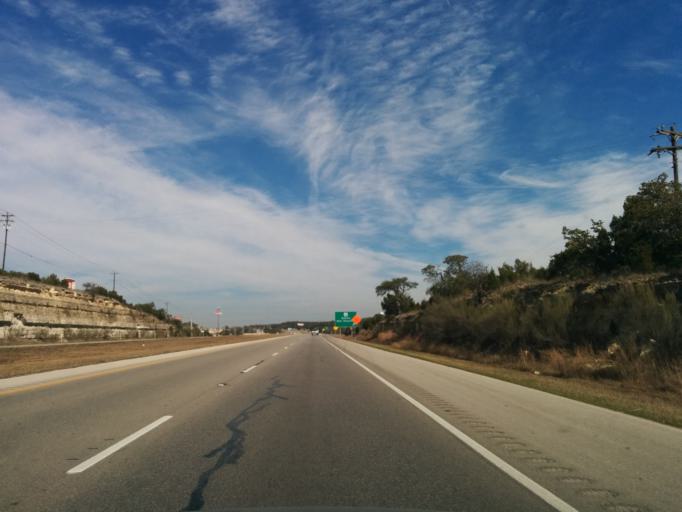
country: US
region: Texas
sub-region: Comal County
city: Bulverde
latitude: 29.7925
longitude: -98.4206
